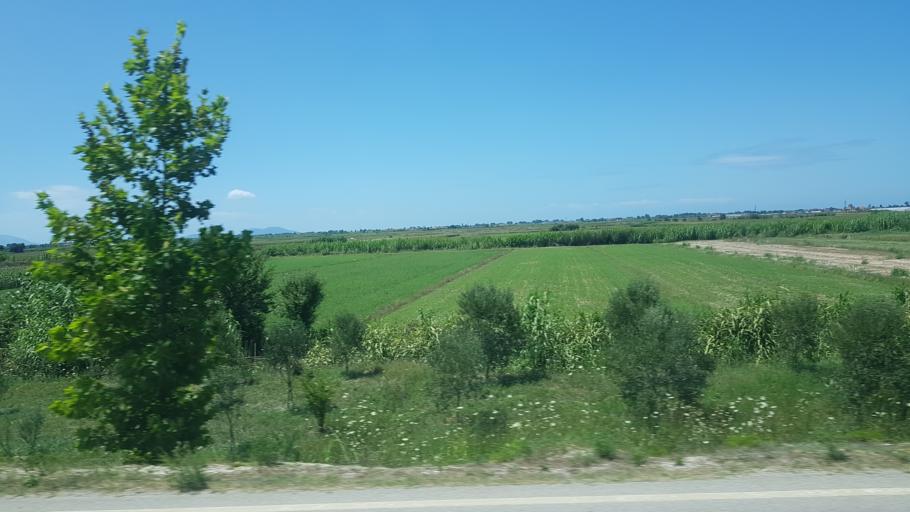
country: AL
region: Fier
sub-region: Rrethi i Fierit
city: Frakulla e Madhe
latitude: 40.6552
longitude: 19.4918
